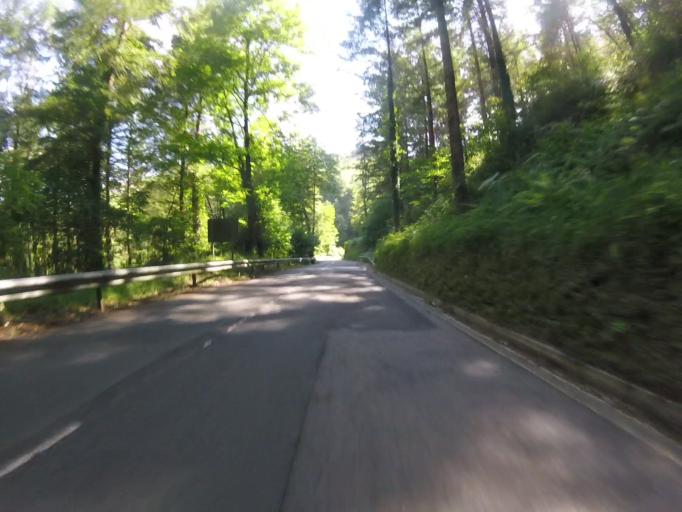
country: ES
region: Basque Country
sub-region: Provincia de Guipuzcoa
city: Beizama
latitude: 43.0965
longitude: -2.2352
